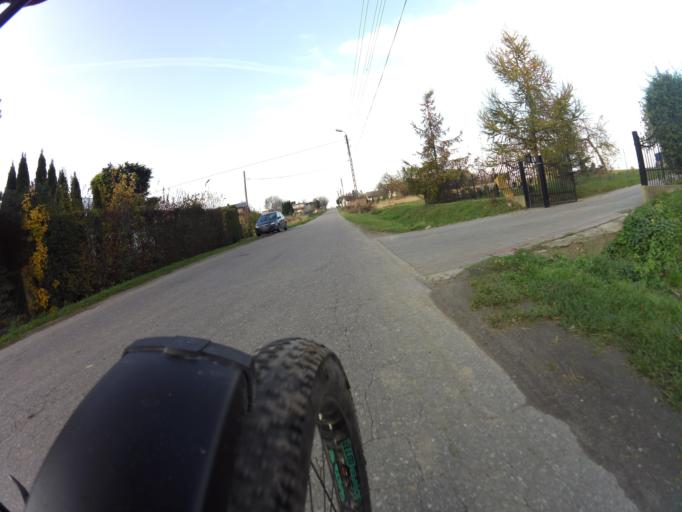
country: PL
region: Pomeranian Voivodeship
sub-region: Powiat pucki
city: Krokowa
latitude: 54.7610
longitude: 18.1824
